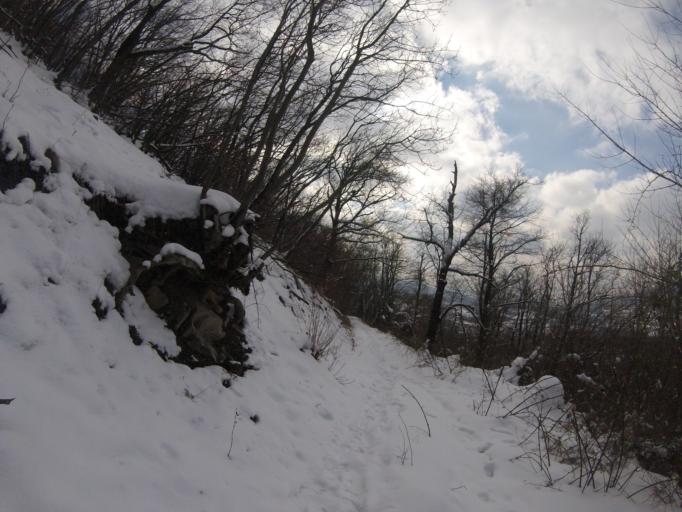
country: HU
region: Pest
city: Pilisszentkereszt
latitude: 47.7029
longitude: 18.9010
